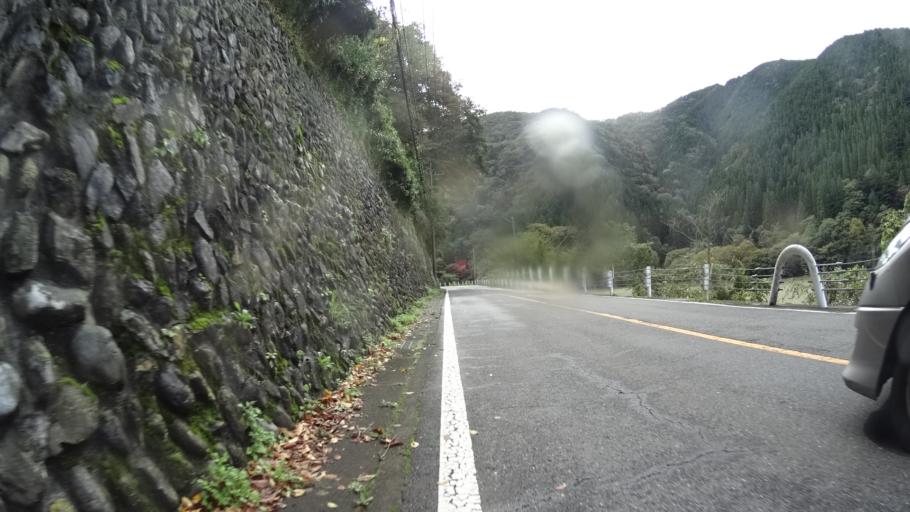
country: JP
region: Yamanashi
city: Otsuki
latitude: 35.7774
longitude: 138.9907
